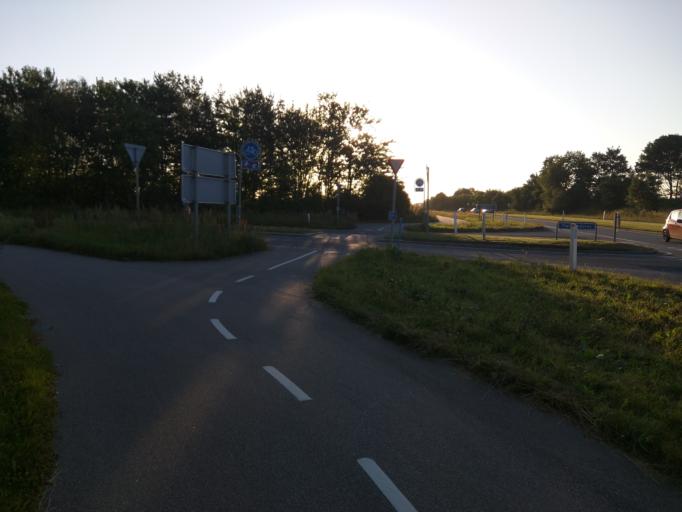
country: DK
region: Central Jutland
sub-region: Viborg Kommune
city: Viborg
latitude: 56.4651
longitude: 9.5024
